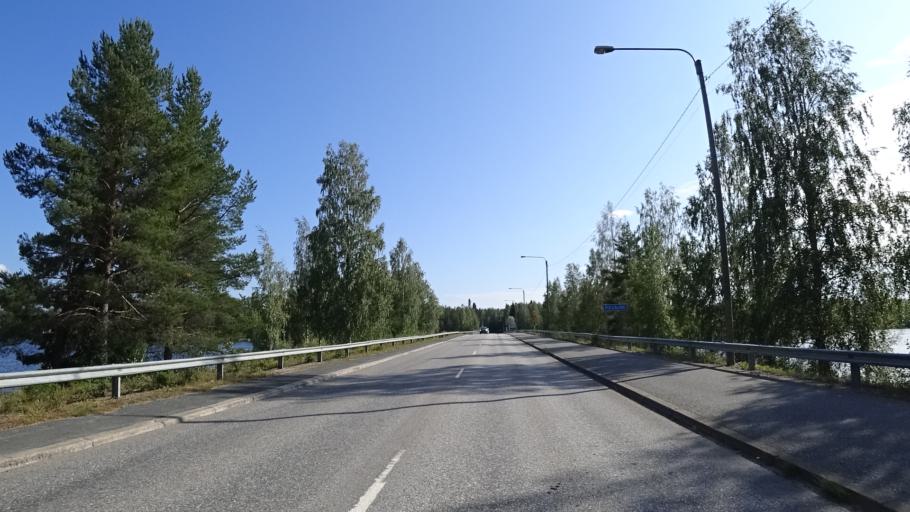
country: FI
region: North Karelia
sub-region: Joensuu
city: Eno
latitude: 62.8049
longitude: 30.1526
